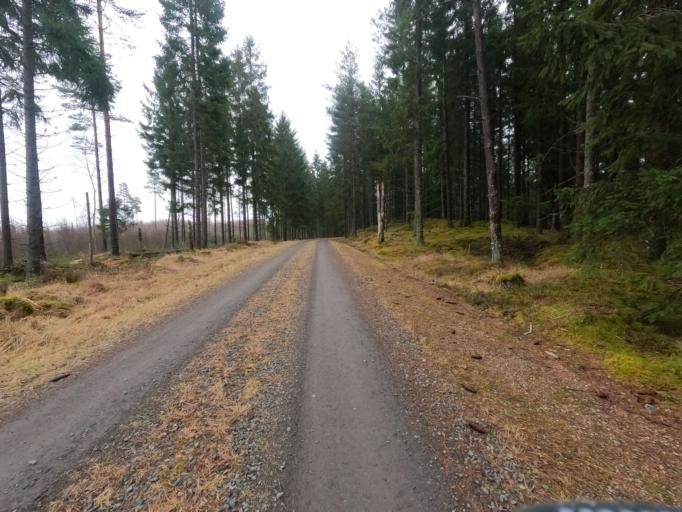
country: SE
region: Kronoberg
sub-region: Markaryds Kommun
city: Stromsnasbruk
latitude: 56.8093
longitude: 13.5680
